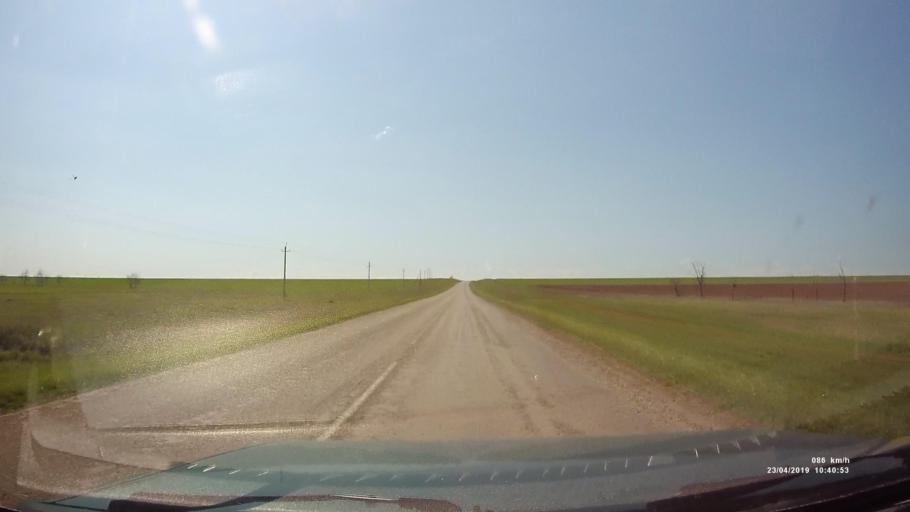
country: RU
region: Kalmykiya
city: Yashalta
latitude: 46.5006
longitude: 42.6384
